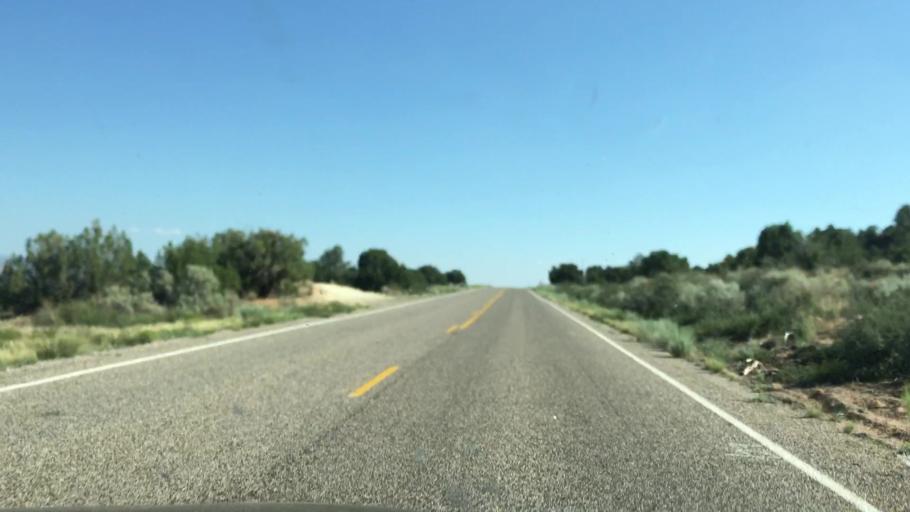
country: US
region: Arizona
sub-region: Coconino County
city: Fredonia
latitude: 36.8757
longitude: -112.7386
